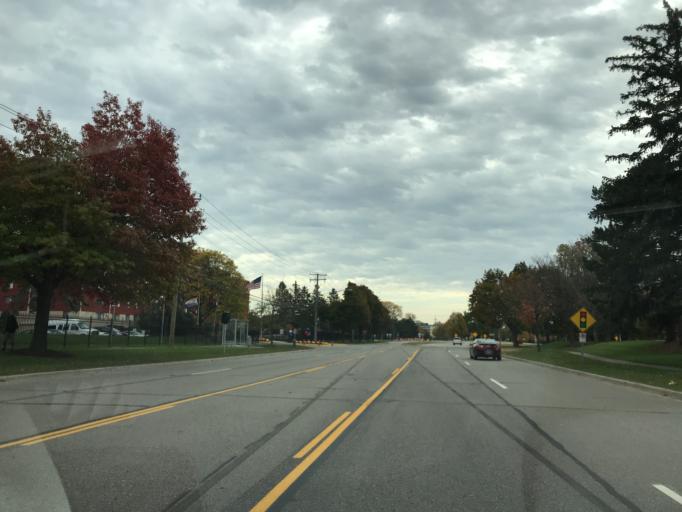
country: US
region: Michigan
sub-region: Oakland County
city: Bingham Farms
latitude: 42.4880
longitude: -83.2928
